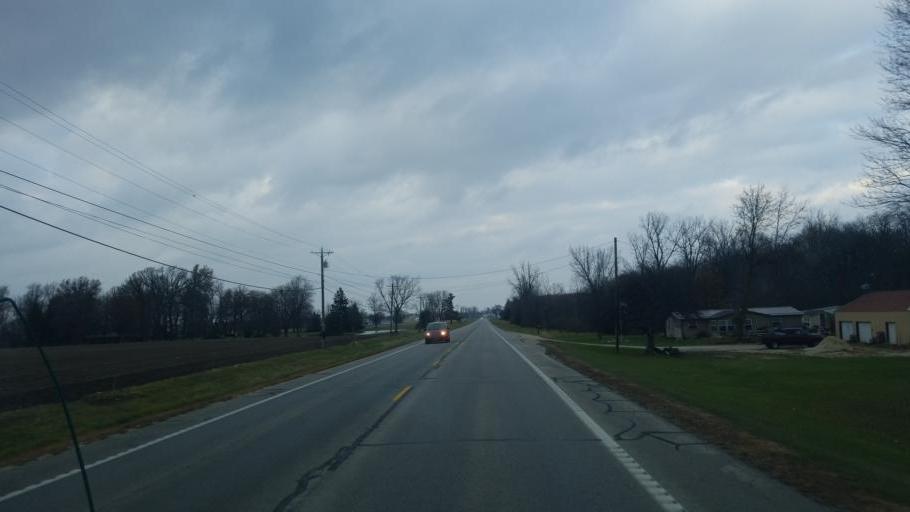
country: US
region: Ohio
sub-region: Mercer County
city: Celina
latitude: 40.5203
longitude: -84.5773
